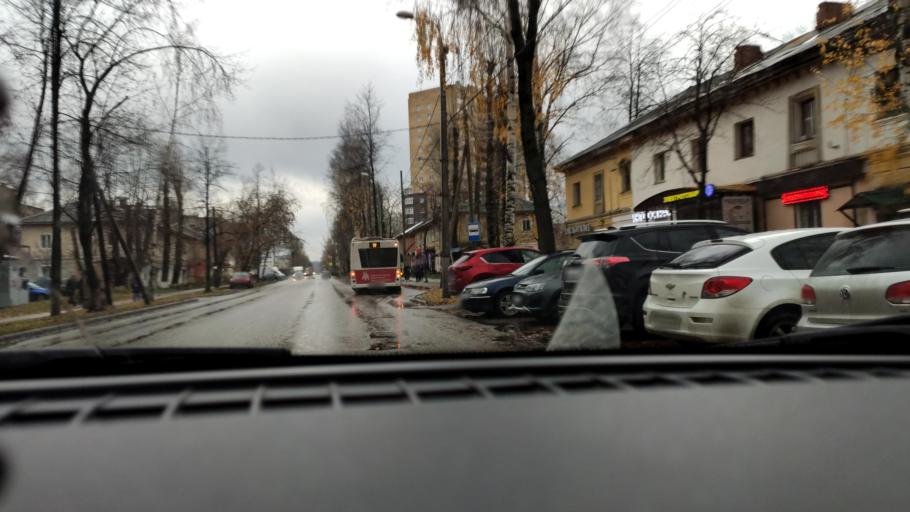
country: RU
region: Perm
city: Perm
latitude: 58.1091
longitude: 56.3773
